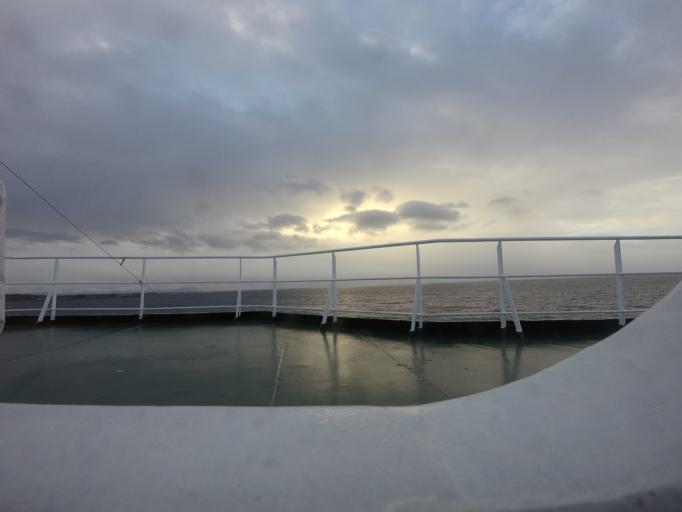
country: NO
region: More og Romsdal
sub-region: Averoy
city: Bruhagen
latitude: 63.1239
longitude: 7.6110
